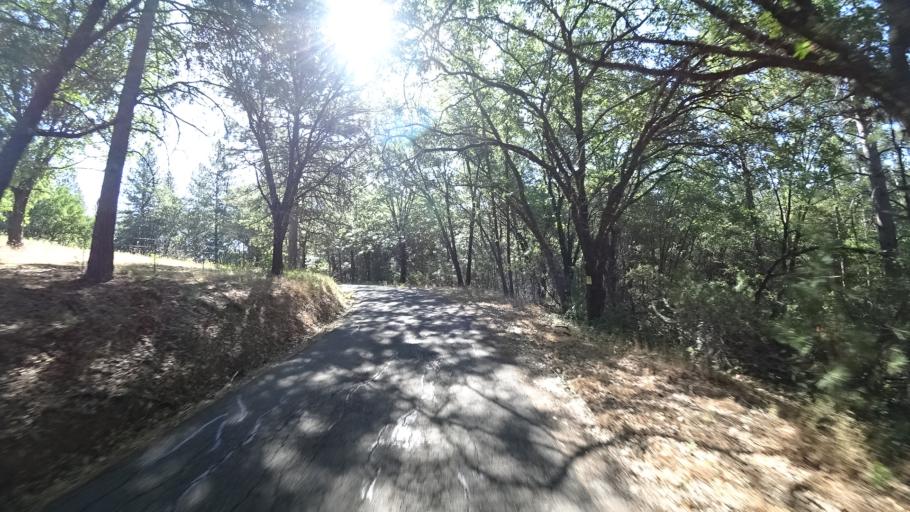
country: US
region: California
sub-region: Amador County
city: Pioneer
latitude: 38.4004
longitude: -120.5520
